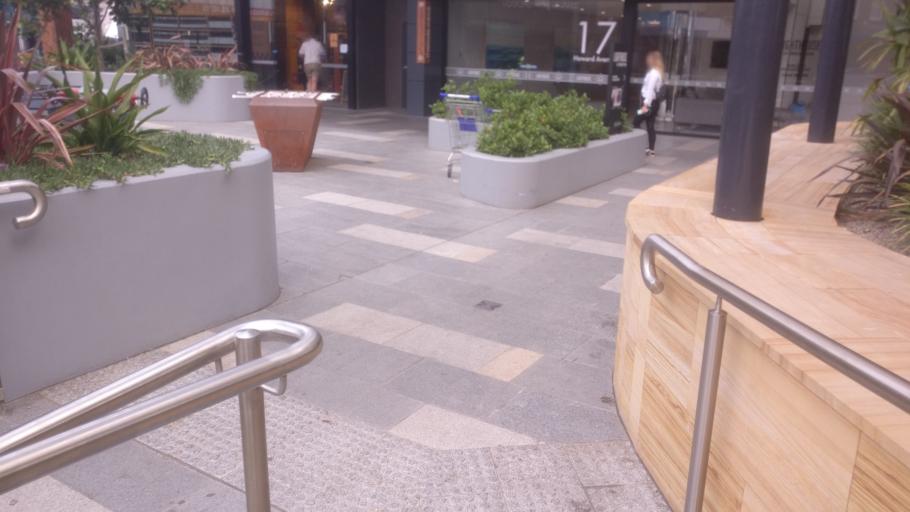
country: AU
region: New South Wales
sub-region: Warringah
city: North Curl Curl
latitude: -33.7527
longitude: 151.2876
